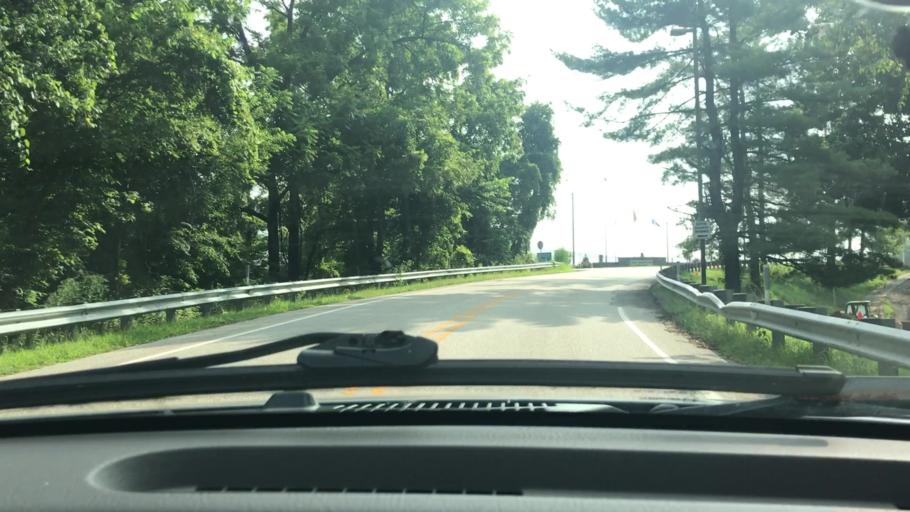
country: US
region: Pennsylvania
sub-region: Dauphin County
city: Middletown
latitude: 40.2058
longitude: -76.7492
